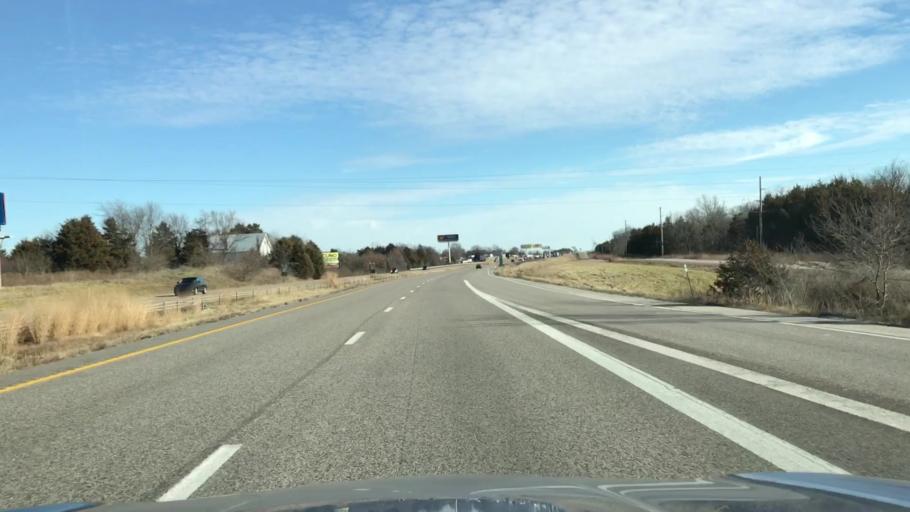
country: US
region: Missouri
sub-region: Montgomery County
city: Montgomery City
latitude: 38.9079
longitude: -91.5368
